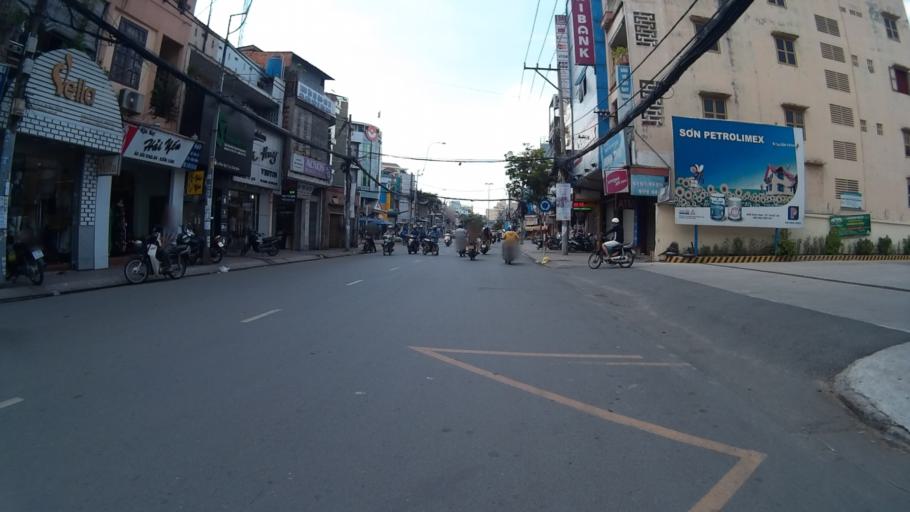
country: VN
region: Ho Chi Minh City
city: Quan Phu Nhuan
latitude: 10.7981
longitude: 106.6632
